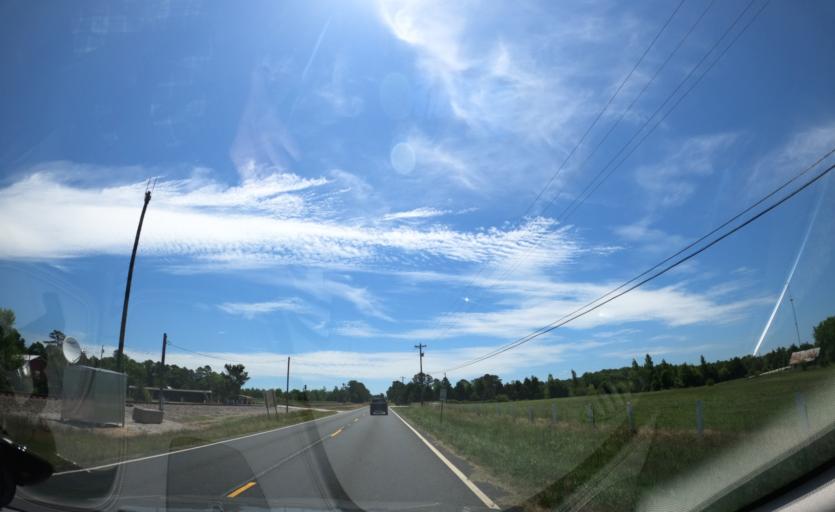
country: US
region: South Carolina
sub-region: McCormick County
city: McCormick
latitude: 33.9242
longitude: -82.3151
